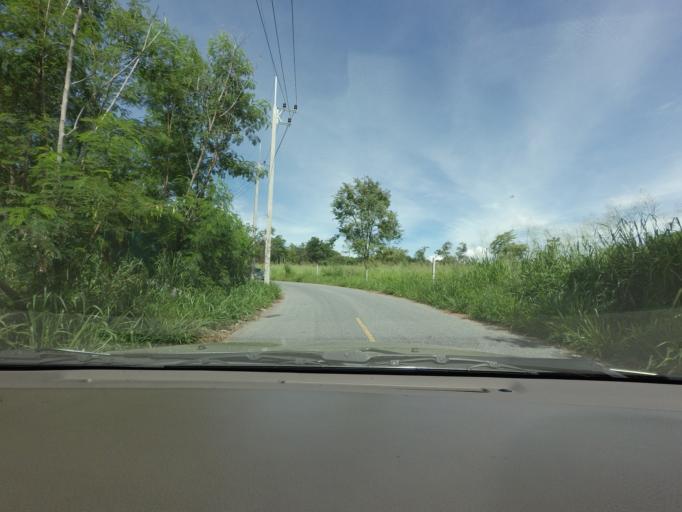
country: TH
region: Chon Buri
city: Si Racha
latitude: 13.2421
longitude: 100.9586
